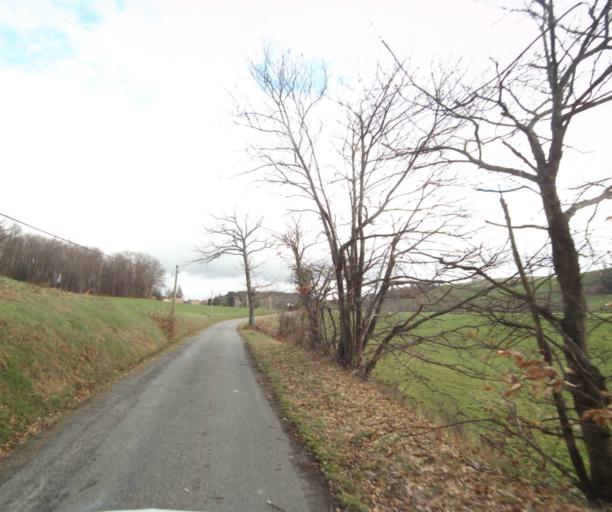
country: FR
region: Rhone-Alpes
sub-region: Departement de la Loire
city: La Talaudiere
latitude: 45.4889
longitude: 4.4146
